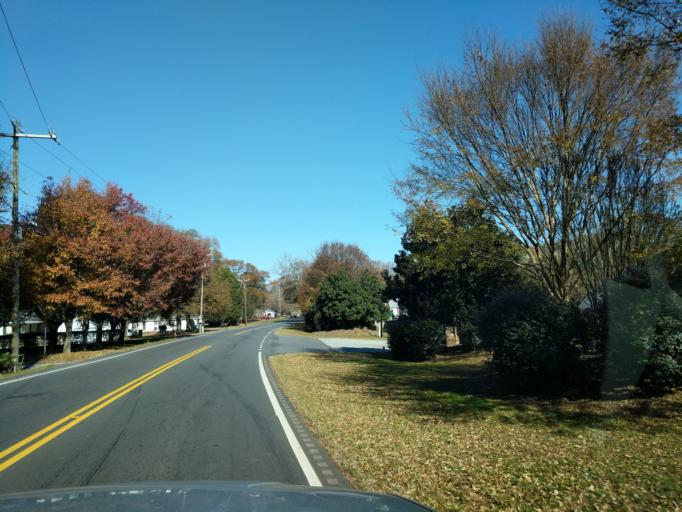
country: US
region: South Carolina
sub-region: Spartanburg County
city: Lyman
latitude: 34.9573
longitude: -82.1433
